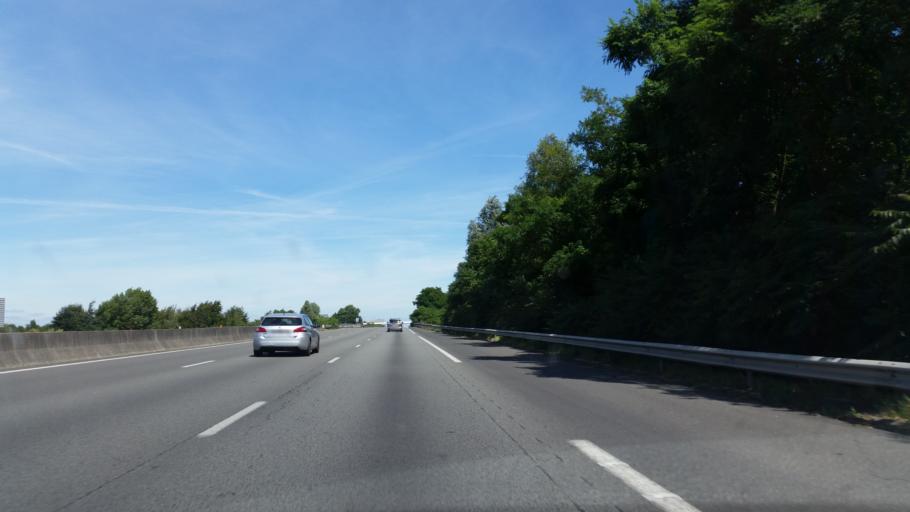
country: FR
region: Nord-Pas-de-Calais
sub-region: Departement du Pas-de-Calais
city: Biache-Saint-Vaast
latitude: 50.3324
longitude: 2.9203
